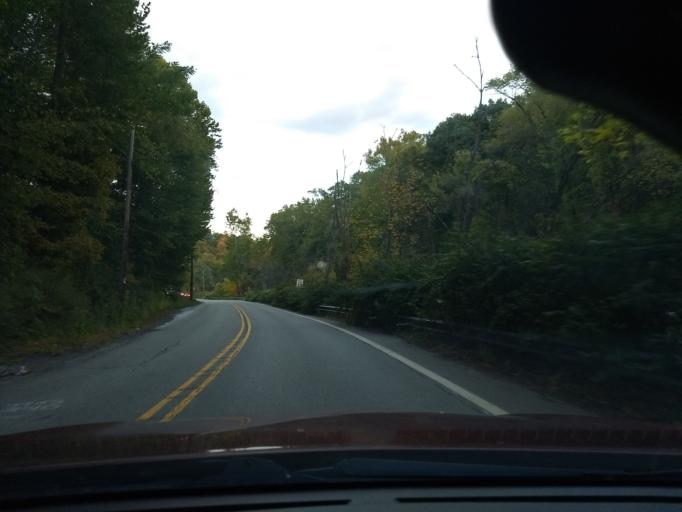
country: US
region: Pennsylvania
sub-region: Allegheny County
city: Brentwood
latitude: 40.3635
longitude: -79.9498
